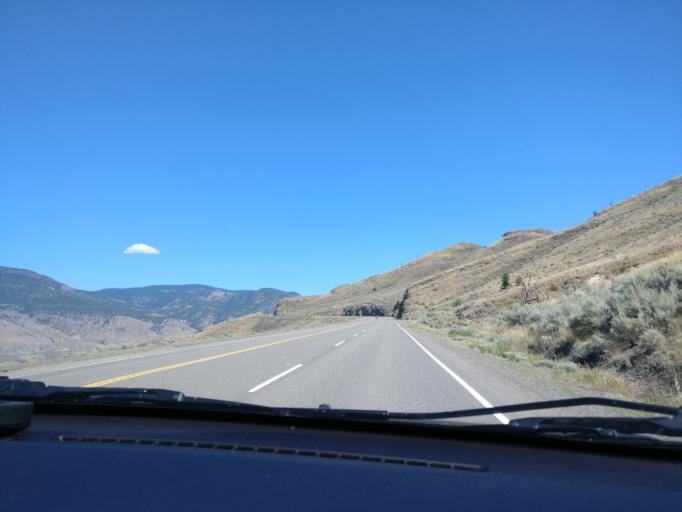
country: CA
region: British Columbia
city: Logan Lake
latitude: 50.7644
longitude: -120.7860
